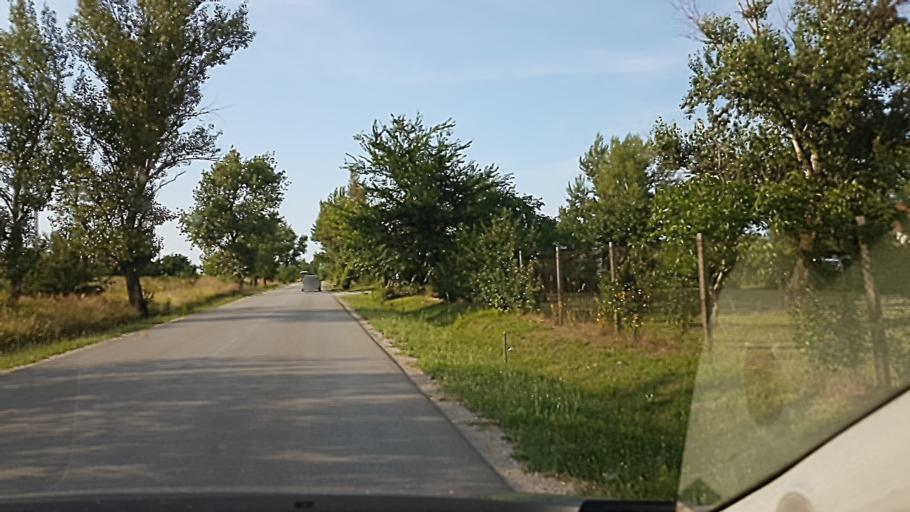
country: HU
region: Pest
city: Dunavarsany
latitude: 47.2590
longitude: 19.0624
